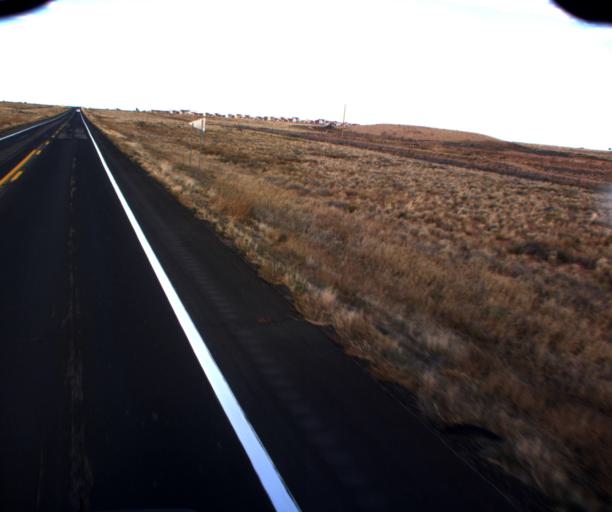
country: US
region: Arizona
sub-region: Apache County
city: Lukachukai
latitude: 36.9593
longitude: -109.3344
